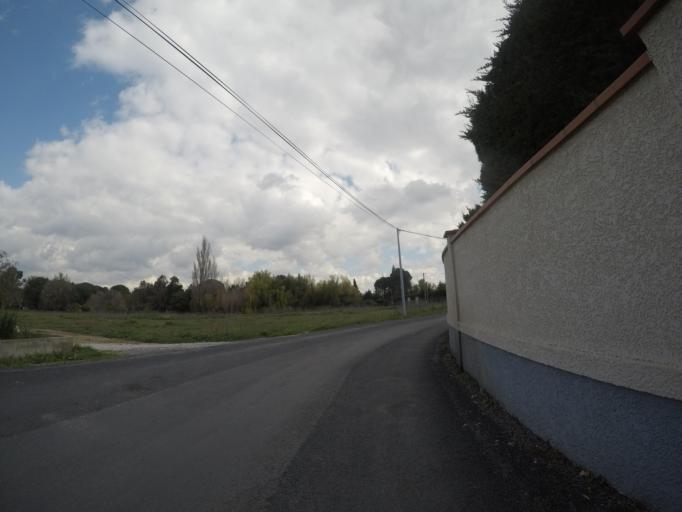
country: FR
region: Languedoc-Roussillon
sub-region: Departement des Pyrenees-Orientales
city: Le Soler
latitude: 42.6734
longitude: 2.7769
